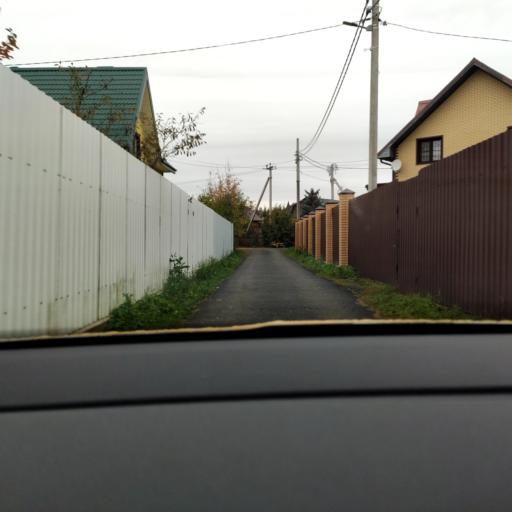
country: RU
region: Moskovskaya
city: Zagoryanskiy
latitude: 55.9644
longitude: 37.9654
